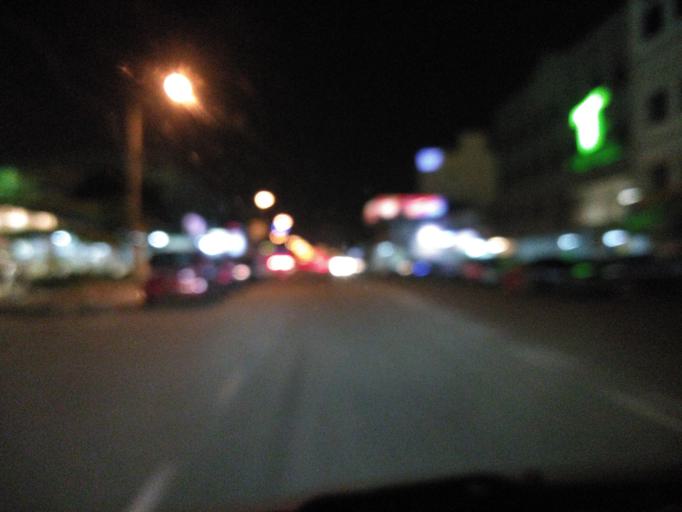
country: MY
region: Penang
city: Butterworth
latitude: 5.4117
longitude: 100.3714
